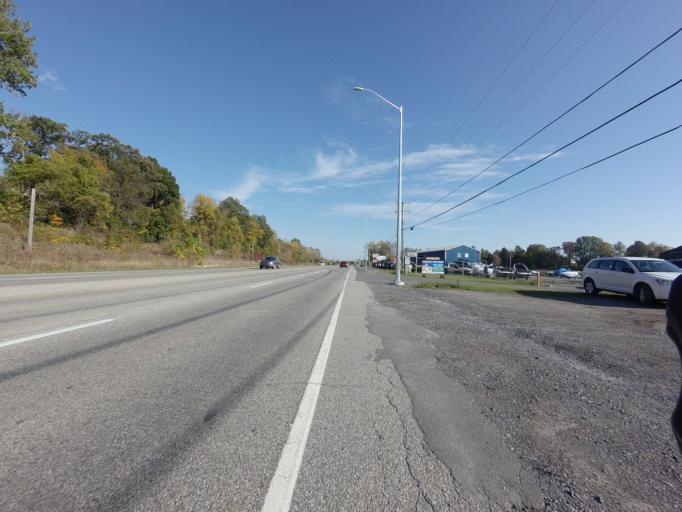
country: CA
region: Ontario
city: Kingston
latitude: 44.2410
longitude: -76.6004
